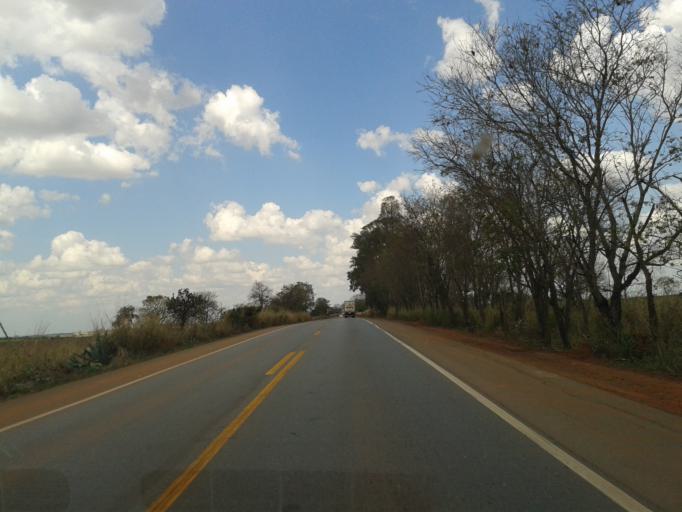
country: BR
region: Minas Gerais
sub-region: Luz
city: Luz
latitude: -19.7834
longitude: -45.7220
